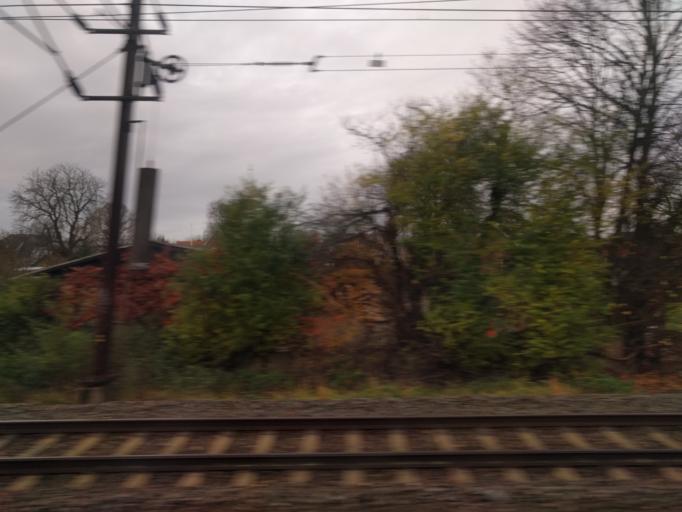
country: DK
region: Zealand
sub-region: Roskilde Kommune
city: Roskilde
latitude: 55.6296
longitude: 12.0701
